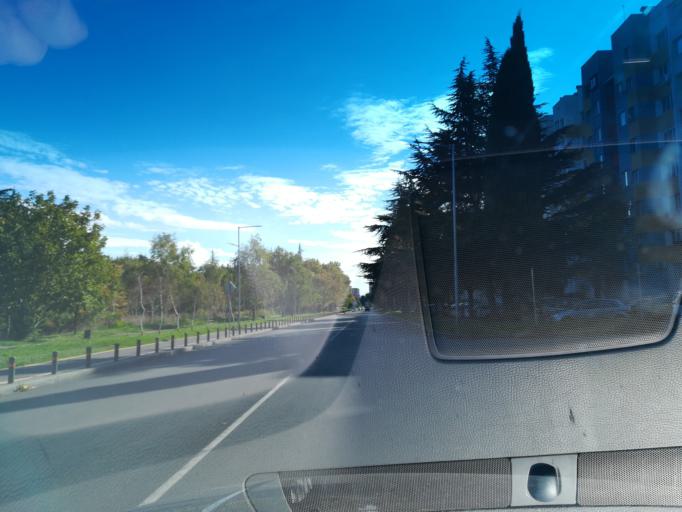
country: BG
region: Stara Zagora
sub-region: Obshtina Stara Zagora
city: Stara Zagora
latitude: 42.4374
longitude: 25.6360
